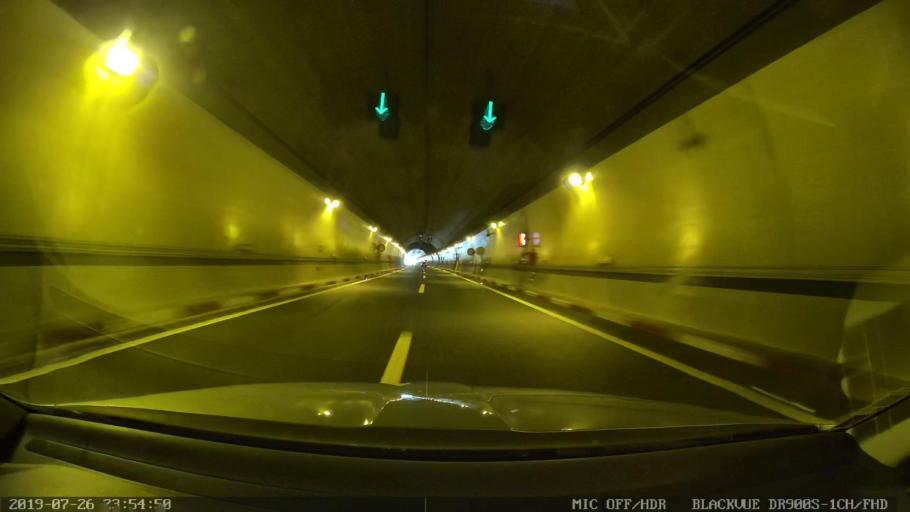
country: ES
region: Extremadura
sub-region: Provincia de Caceres
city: Higuera
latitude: 39.6941
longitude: -5.7004
